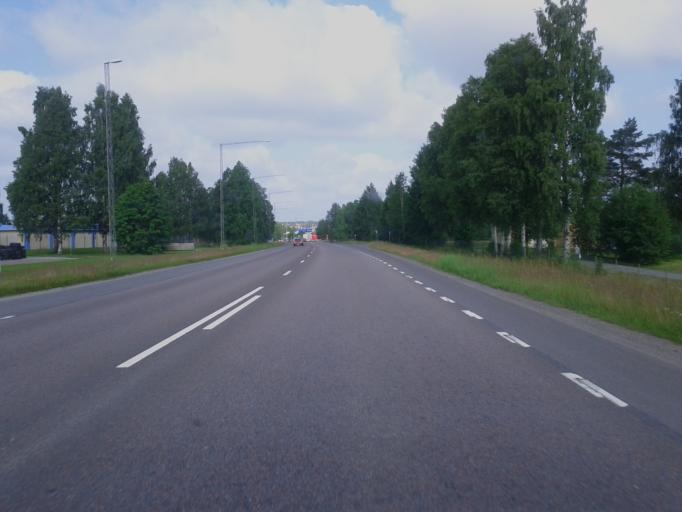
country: SE
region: Vaesterbotten
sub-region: Skelleftea Kommun
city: Skelleftea
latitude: 64.7396
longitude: 20.9641
